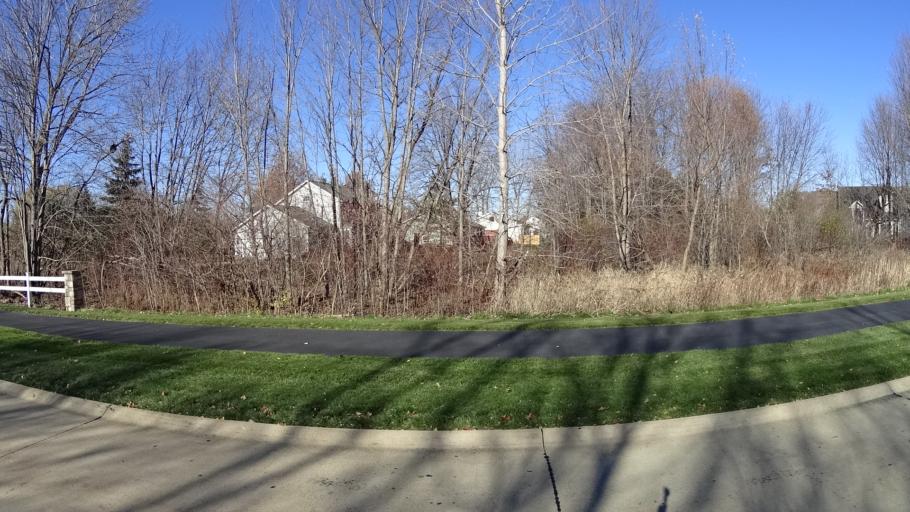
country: US
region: Ohio
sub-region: Lorain County
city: Avon Center
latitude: 41.4325
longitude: -82.0024
